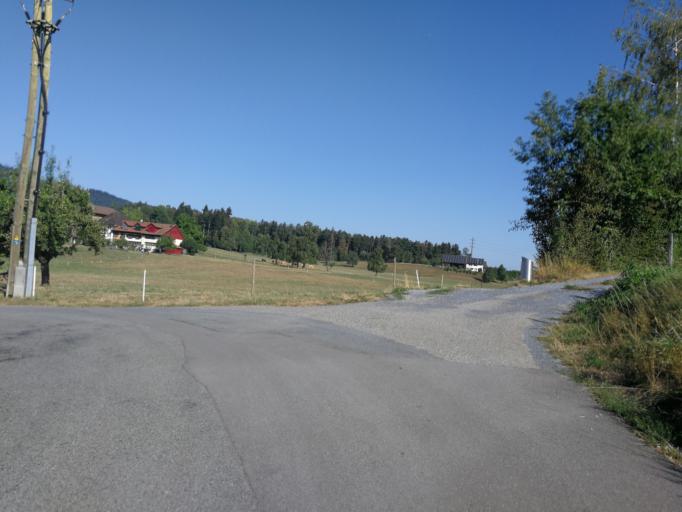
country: CH
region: Zurich
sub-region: Bezirk Uster
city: Esslingen
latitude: 47.2925
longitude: 8.7092
